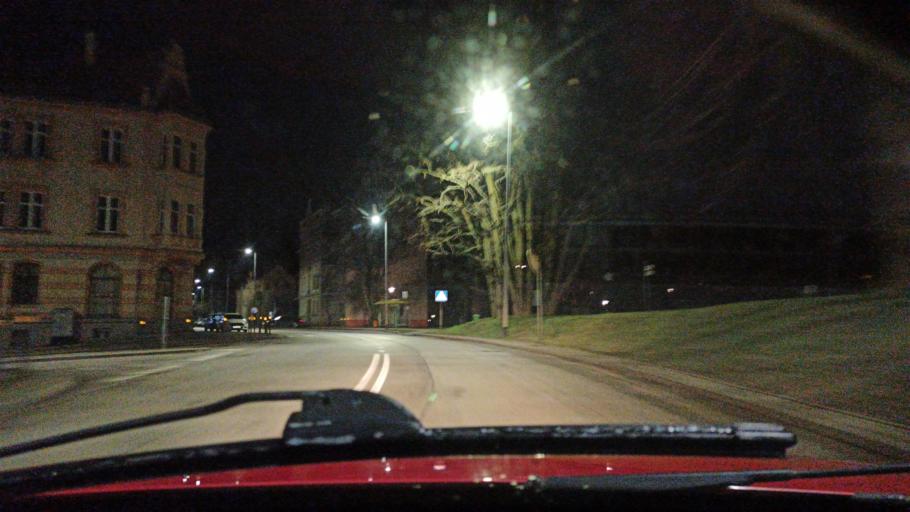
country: PL
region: Warmian-Masurian Voivodeship
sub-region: Powiat elblaski
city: Elblag
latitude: 54.1603
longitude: 19.4104
